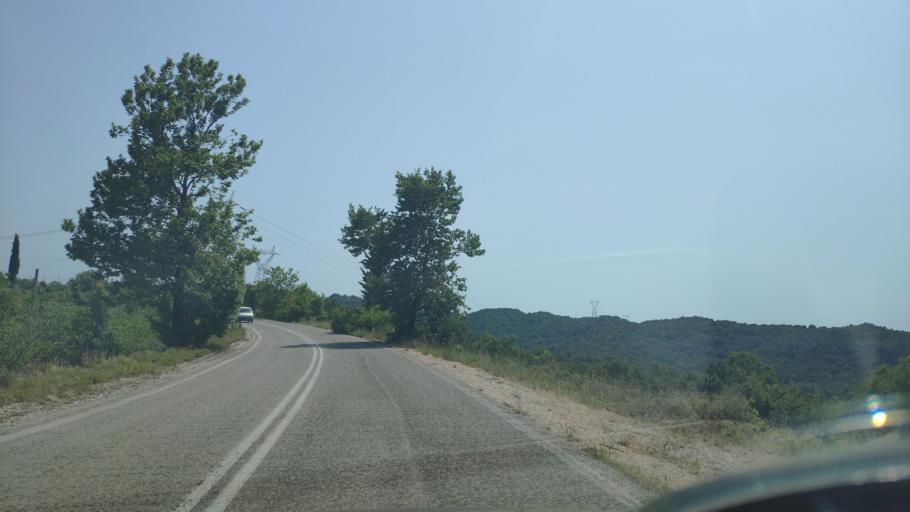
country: GR
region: Epirus
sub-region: Nomos Artas
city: Ano Kalentini
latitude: 39.2100
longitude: 21.1165
